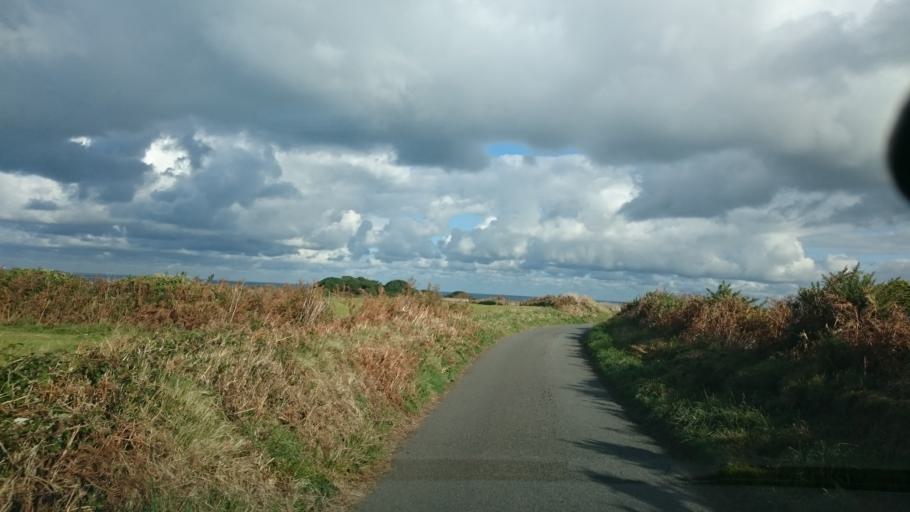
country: GG
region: St Peter Port
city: Saint Peter Port
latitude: 49.4305
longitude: -2.6679
